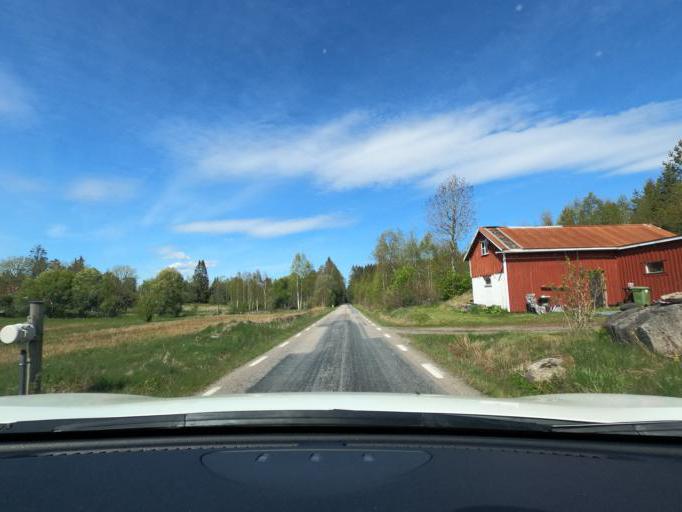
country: SE
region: Vaestra Goetaland
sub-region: Marks Kommun
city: Horred
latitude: 57.4418
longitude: 12.4310
